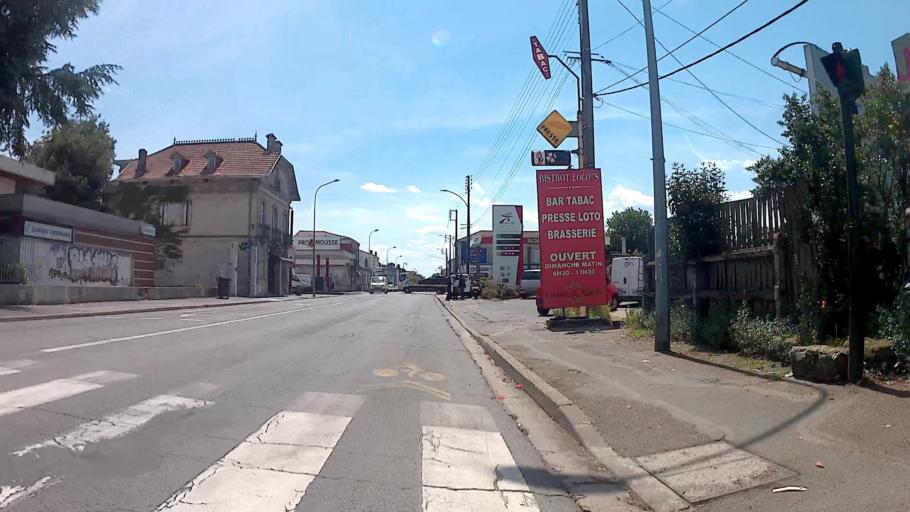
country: FR
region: Aquitaine
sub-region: Departement de la Gironde
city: Talence
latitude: 44.8146
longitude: -0.5776
